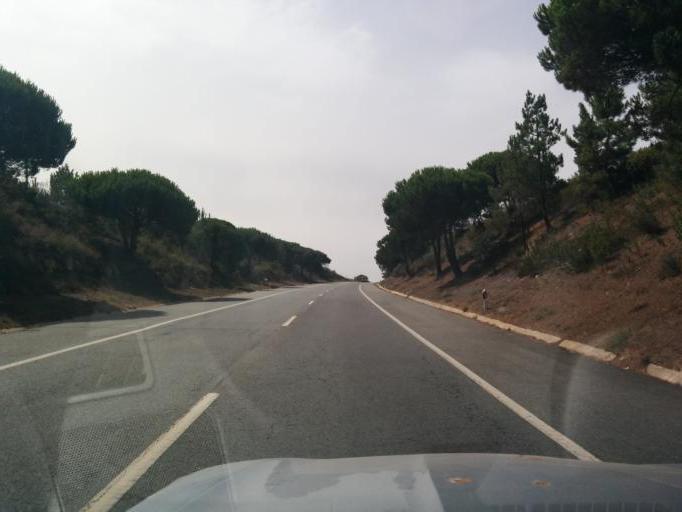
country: PT
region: Beja
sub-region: Odemira
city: Vila Nova de Milfontes
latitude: 37.7202
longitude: -8.7670
